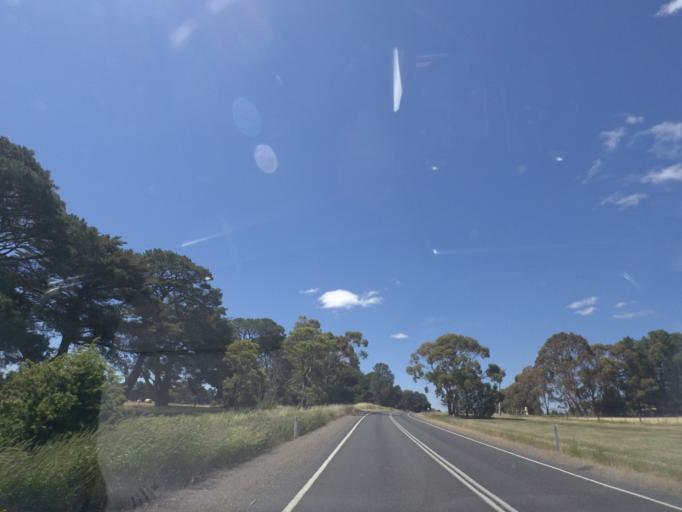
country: AU
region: Victoria
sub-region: Mount Alexander
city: Castlemaine
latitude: -37.2327
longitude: 144.3309
